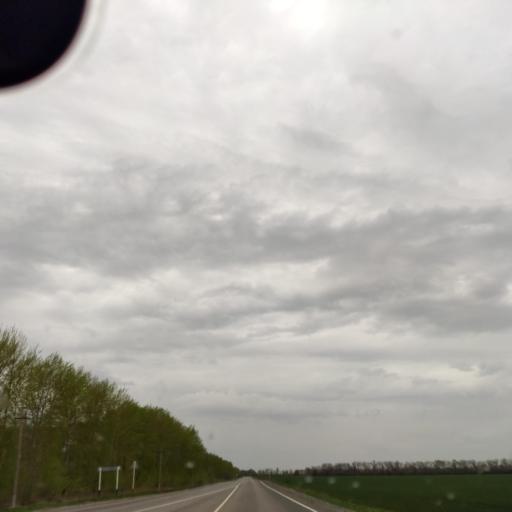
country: RU
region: Voronezj
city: Latnaya
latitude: 51.7053
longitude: 38.7880
